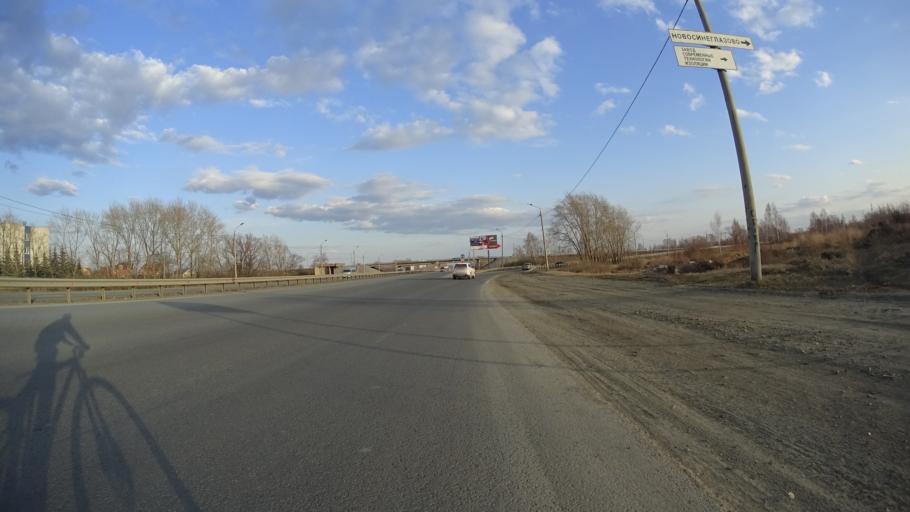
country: RU
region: Chelyabinsk
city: Novosineglazovskiy
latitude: 55.0638
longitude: 61.3979
